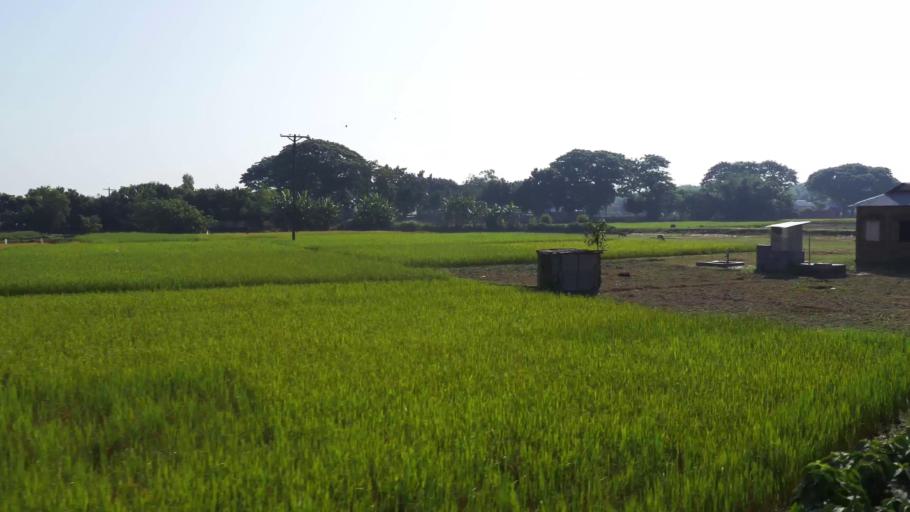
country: BD
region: Dhaka
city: Muktagacha
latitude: 24.7954
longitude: 90.3149
